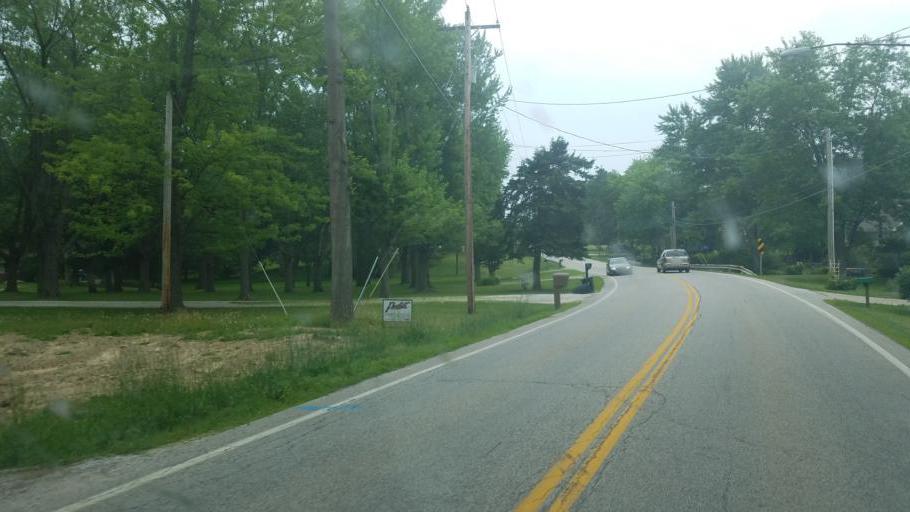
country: US
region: Ohio
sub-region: Summit County
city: Tallmadge
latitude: 41.0771
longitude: -81.4169
